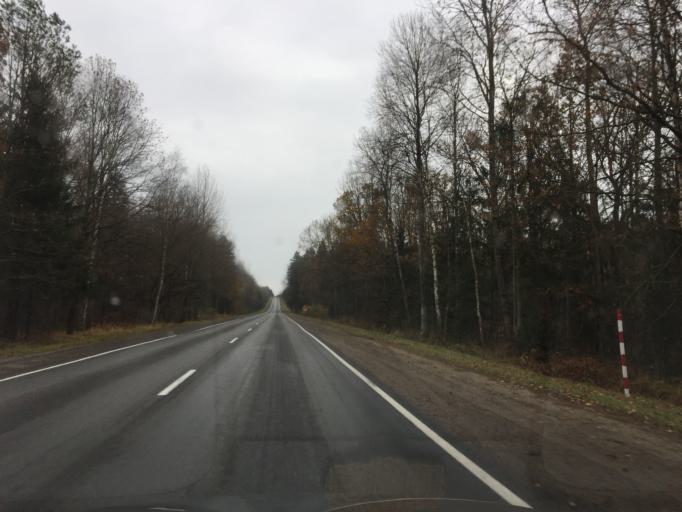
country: BY
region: Mogilev
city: Chavusy
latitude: 53.7715
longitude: 31.0523
